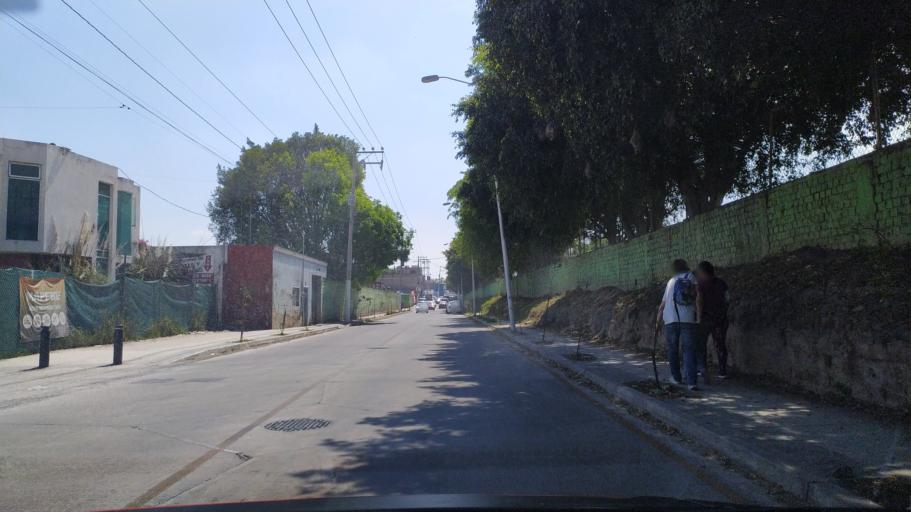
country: MX
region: Jalisco
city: Nuevo Mexico
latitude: 20.7692
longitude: -103.4378
